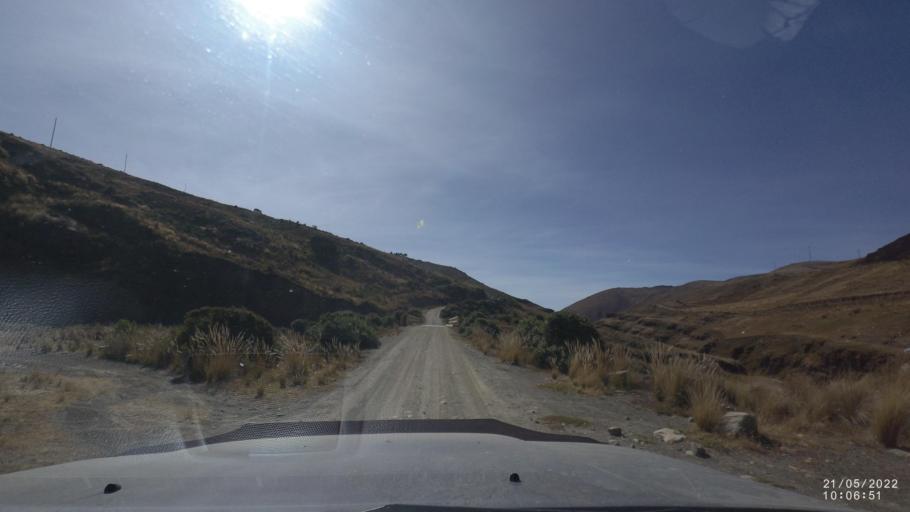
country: BO
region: Cochabamba
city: Colomi
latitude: -17.3385
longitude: -65.9884
